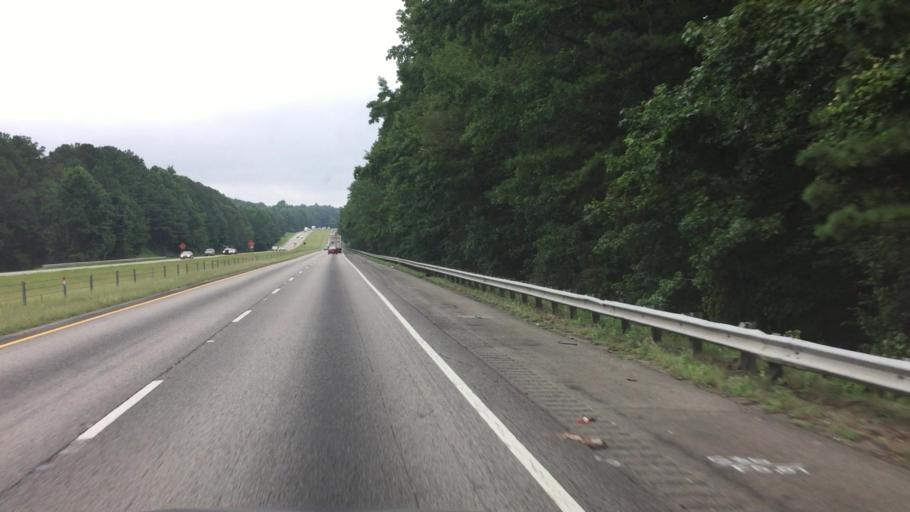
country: US
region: Georgia
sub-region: Barrow County
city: Auburn
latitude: 34.0801
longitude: -83.8804
